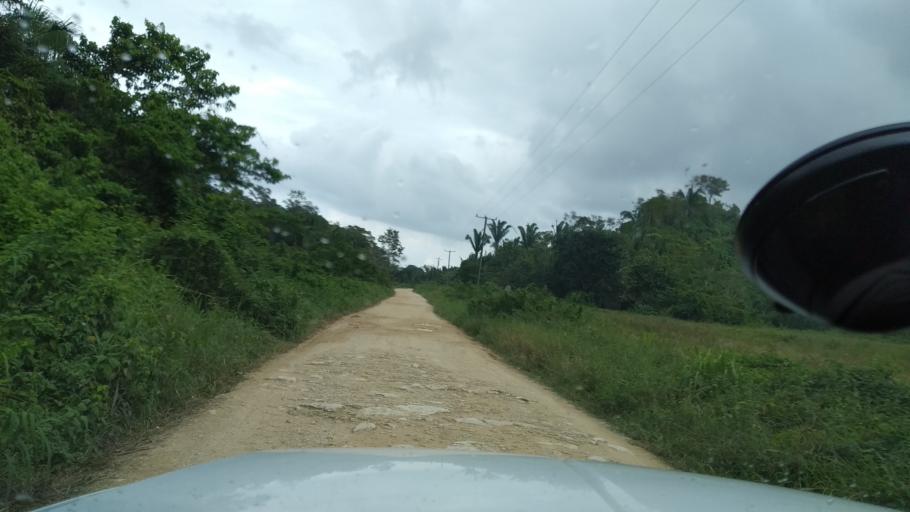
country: BZ
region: Toledo
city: Punta Gorda
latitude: 16.2018
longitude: -89.0371
